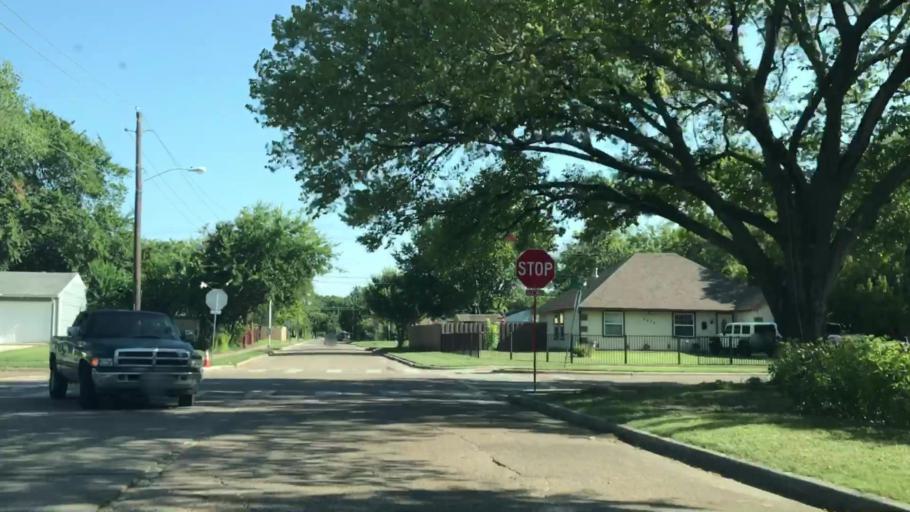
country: US
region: Texas
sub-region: Dallas County
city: Mesquite
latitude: 32.8250
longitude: -96.6713
